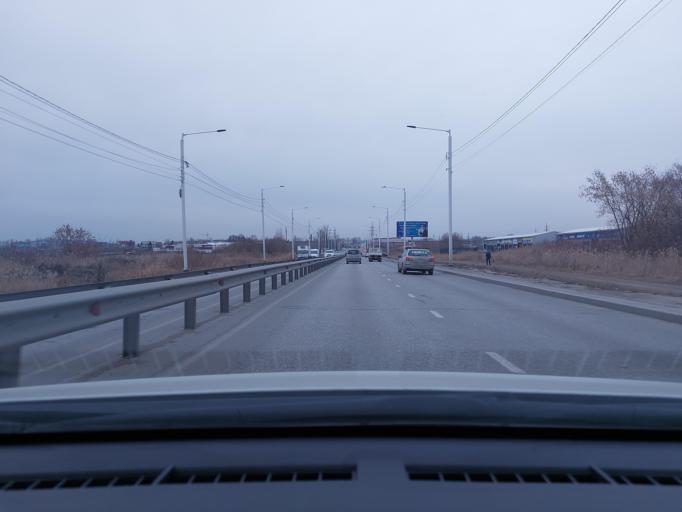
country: RU
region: Irkutsk
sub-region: Irkutskiy Rayon
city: Irkutsk
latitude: 52.3325
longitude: 104.2336
